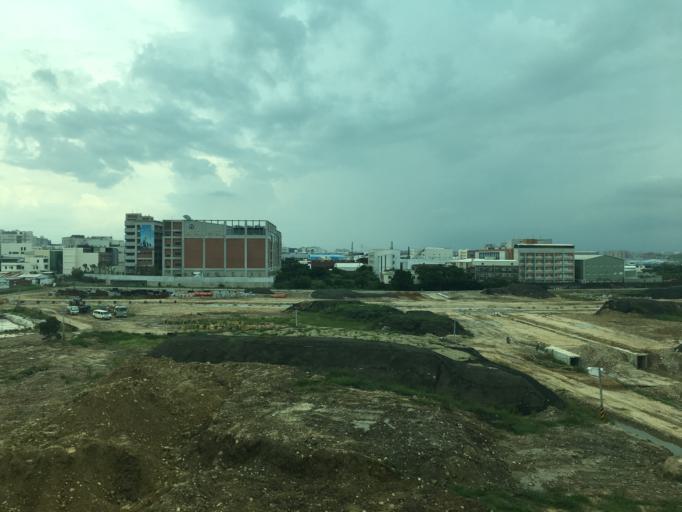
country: TW
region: Taiwan
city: Taoyuan City
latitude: 25.0808
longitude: 121.2836
